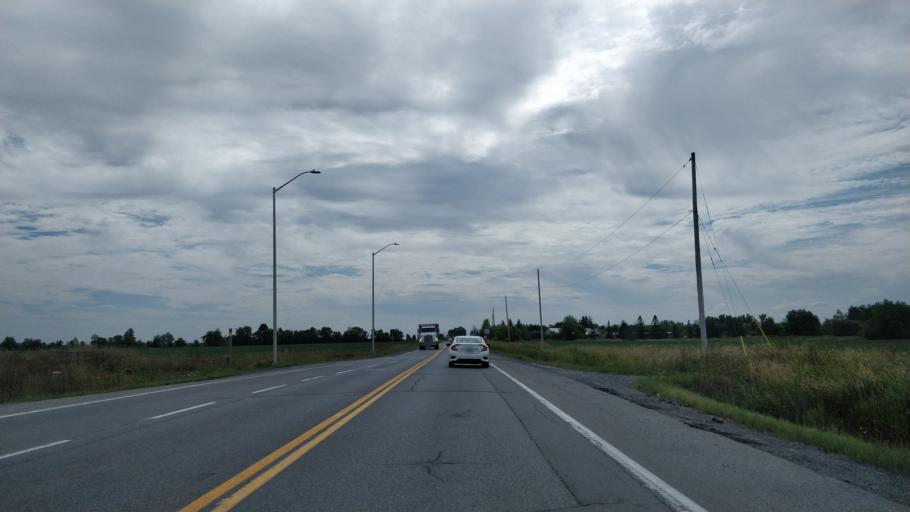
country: CA
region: Ontario
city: Bells Corners
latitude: 45.2691
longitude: -75.8575
